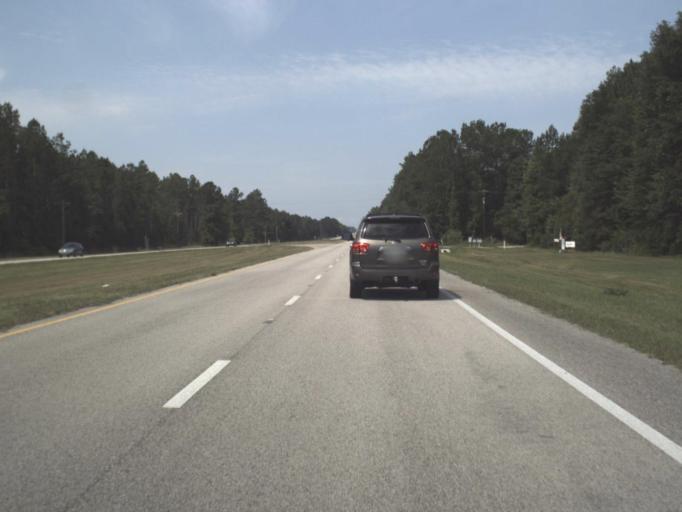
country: US
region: Florida
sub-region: Alachua County
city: Waldo
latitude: 29.7488
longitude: -82.2241
